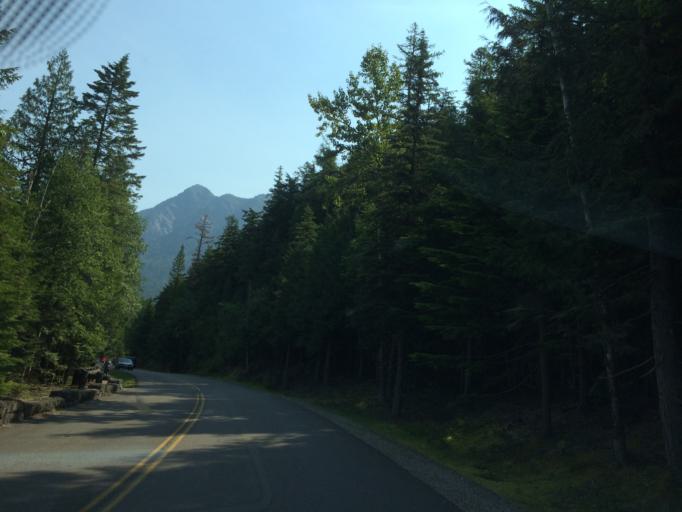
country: US
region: Montana
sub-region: Flathead County
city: Columbia Falls
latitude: 48.6409
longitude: -113.8580
